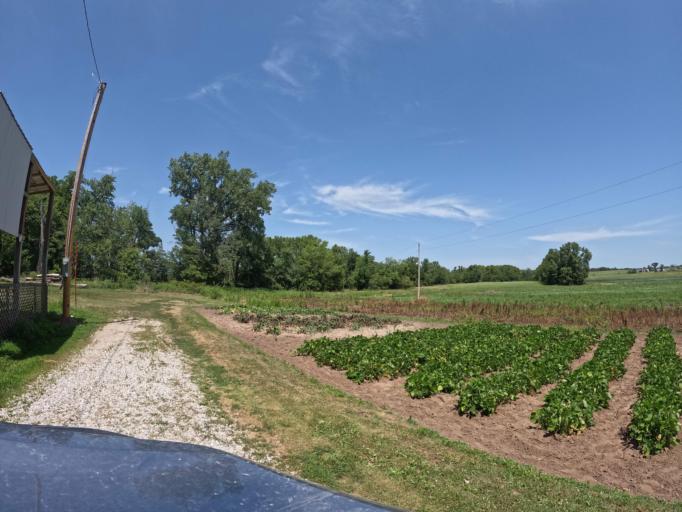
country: US
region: Iowa
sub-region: Henry County
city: Mount Pleasant
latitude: 40.8998
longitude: -91.5594
